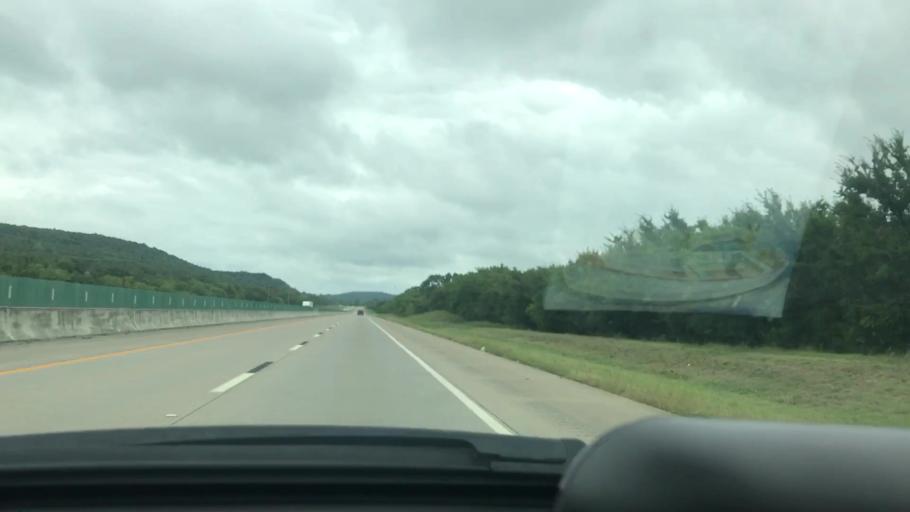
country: US
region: Oklahoma
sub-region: Pittsburg County
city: Krebs
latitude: 35.0783
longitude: -95.7030
